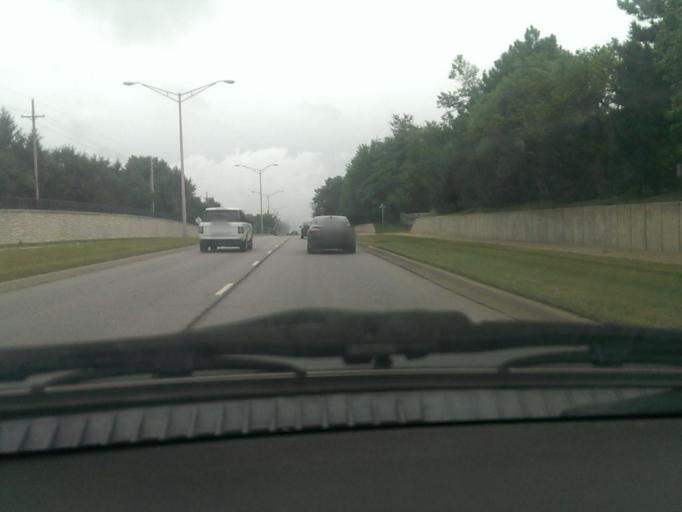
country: US
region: Kansas
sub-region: Johnson County
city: Leawood
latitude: 38.8966
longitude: -94.6493
